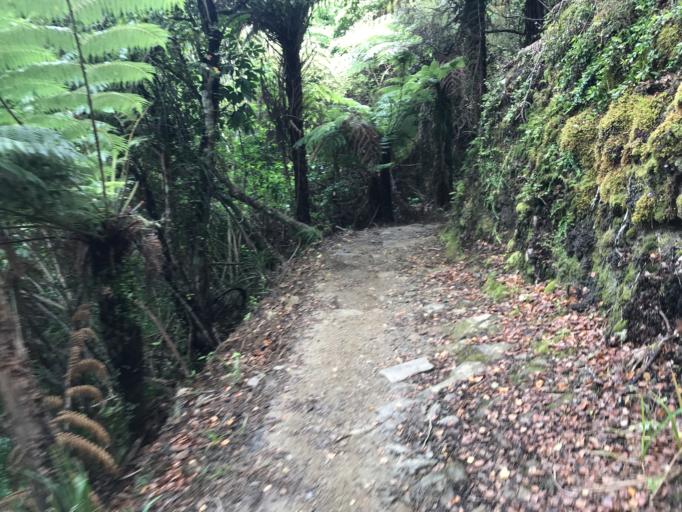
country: NZ
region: Marlborough
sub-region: Marlborough District
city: Picton
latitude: -41.2510
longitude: 173.9528
